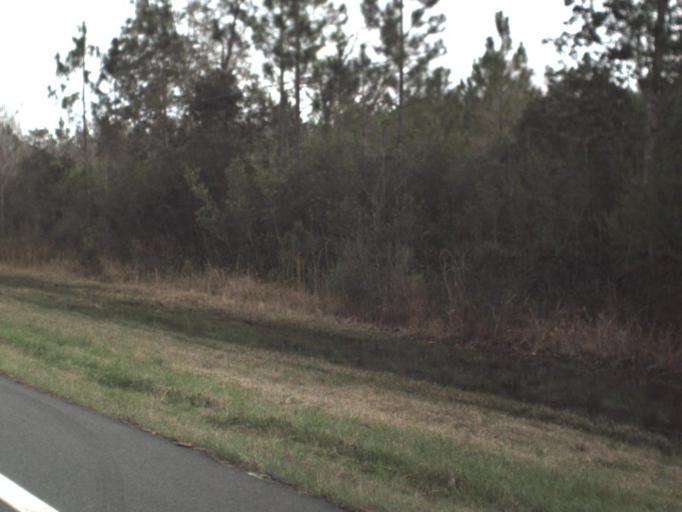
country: US
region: Florida
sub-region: Gulf County
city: Wewahitchka
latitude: 30.1394
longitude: -85.2553
